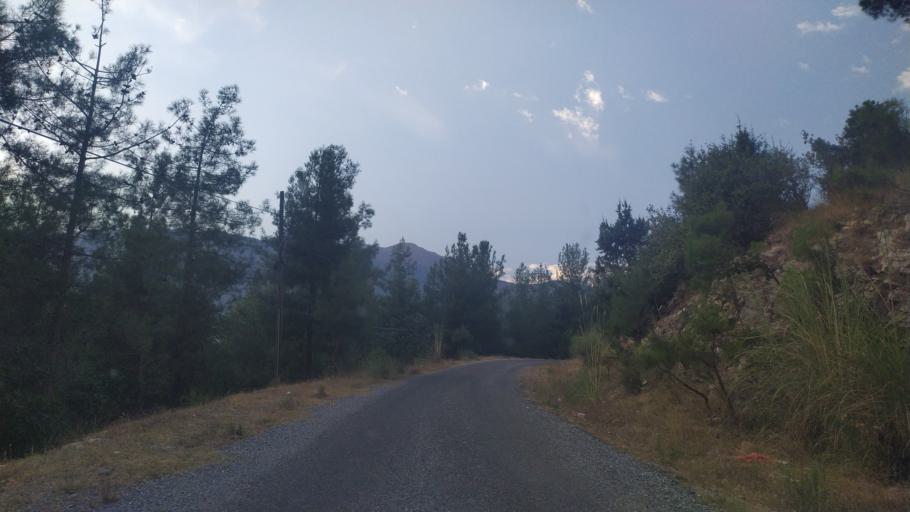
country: TR
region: Mersin
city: Camliyayla
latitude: 37.2224
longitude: 34.7101
